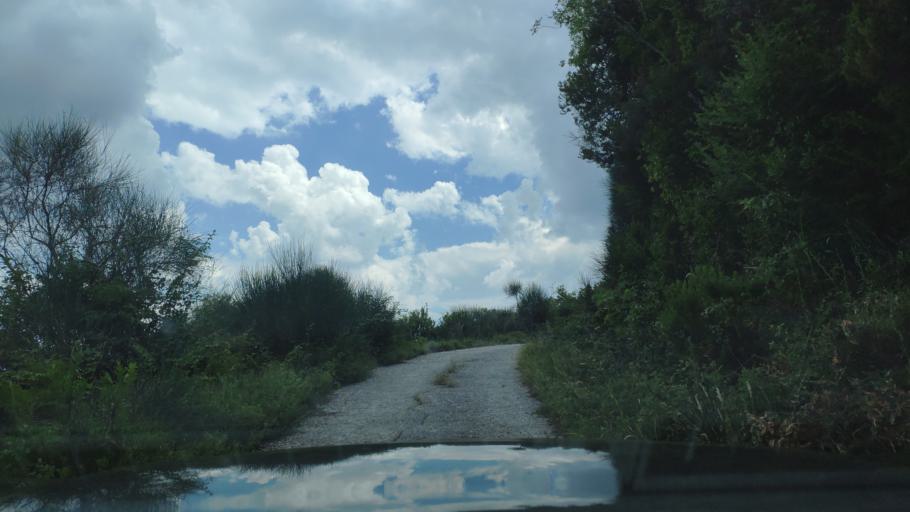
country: GR
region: Epirus
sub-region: Nomos Artas
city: Agios Dimitrios
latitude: 39.3207
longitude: 21.0022
